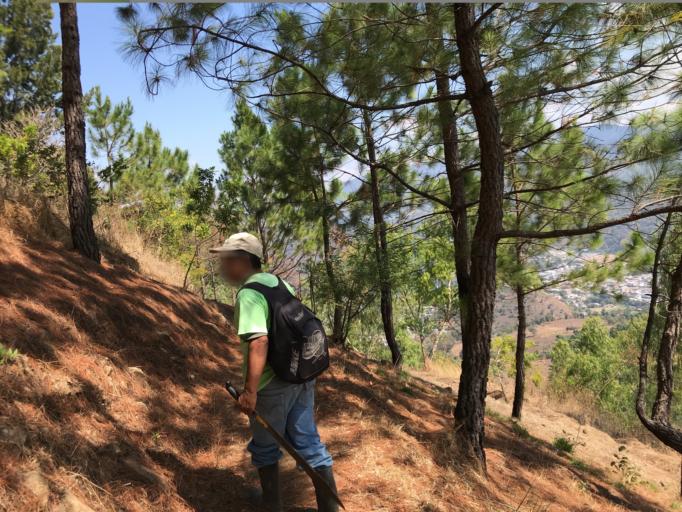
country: GT
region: Guatemala
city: Villa Canales
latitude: 14.4782
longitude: -90.5461
